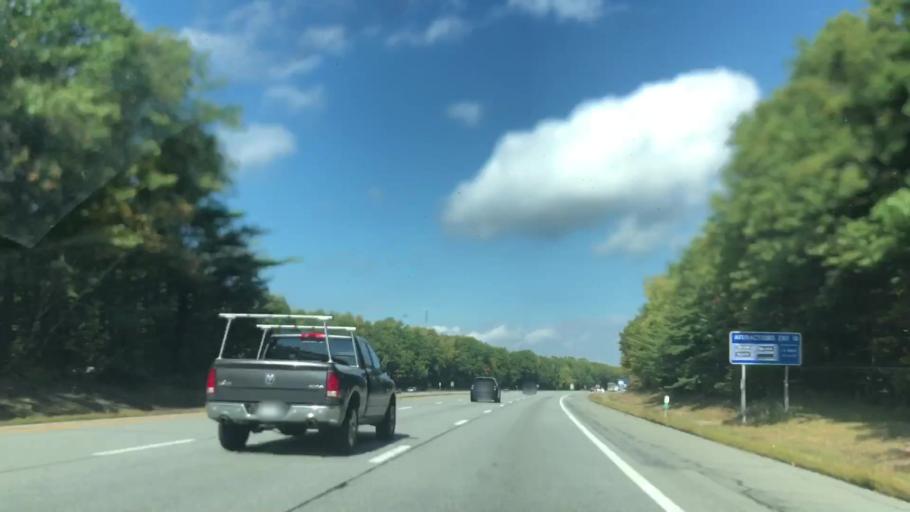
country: US
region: New York
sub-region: Warren County
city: West Glens Falls
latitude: 43.2855
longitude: -73.6807
